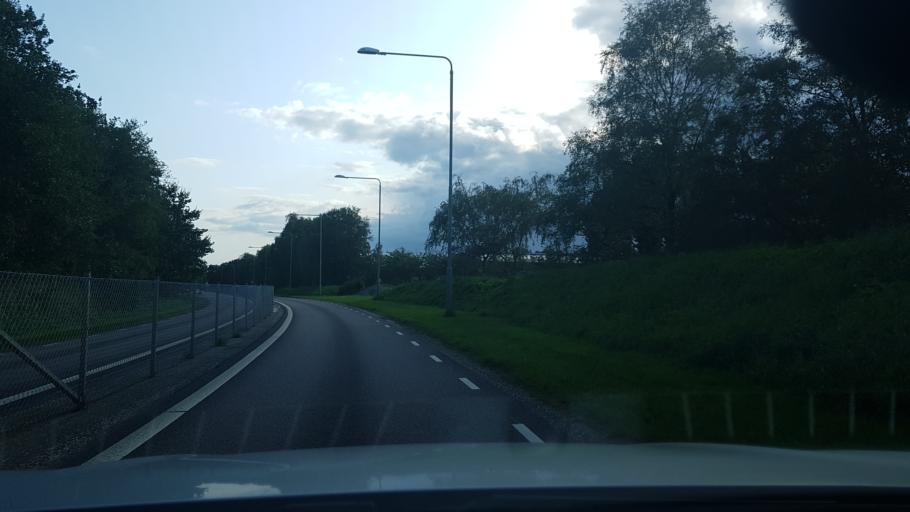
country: SE
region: Vaestra Goetaland
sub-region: Goteborg
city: Majorna
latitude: 57.6538
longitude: 11.8703
